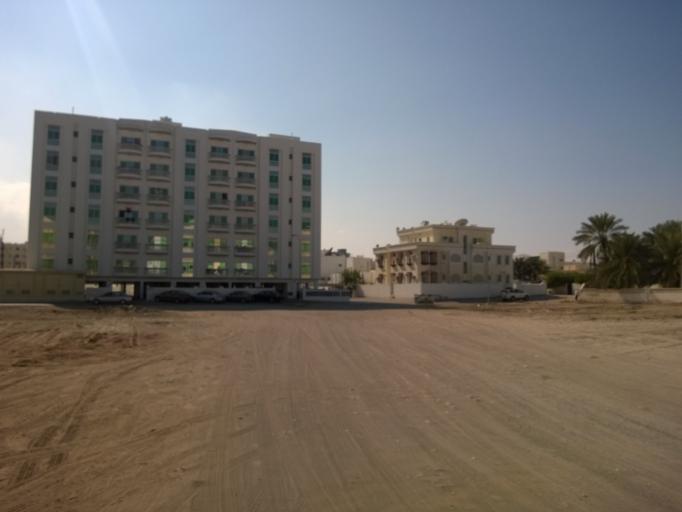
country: OM
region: Muhafazat Masqat
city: Bawshar
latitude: 23.5901
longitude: 58.4270
